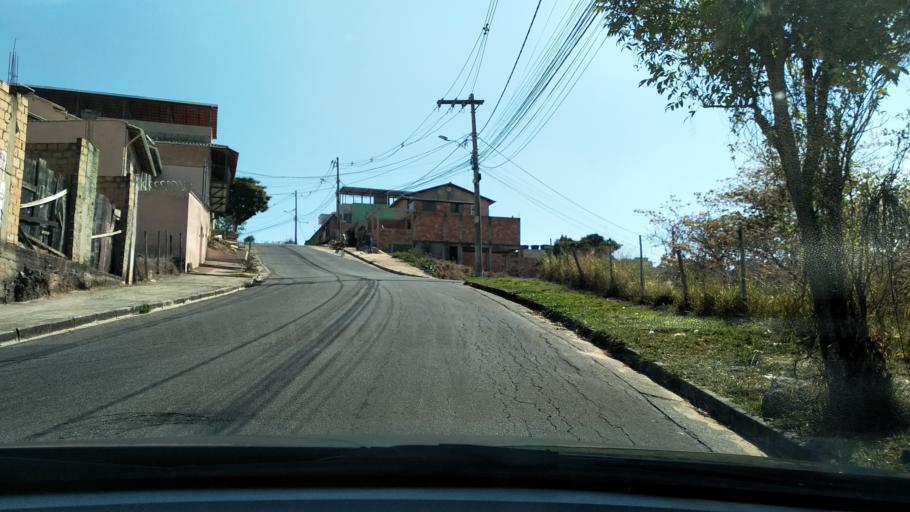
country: BR
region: Minas Gerais
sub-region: Belo Horizonte
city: Belo Horizonte
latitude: -19.8606
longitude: -43.8767
